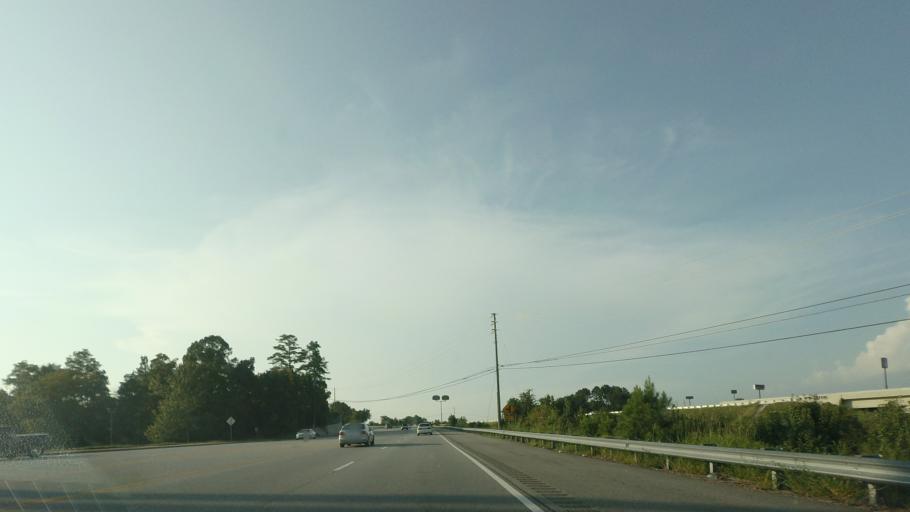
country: US
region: Georgia
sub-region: Bibb County
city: Macon
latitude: 32.9020
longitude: -83.6874
